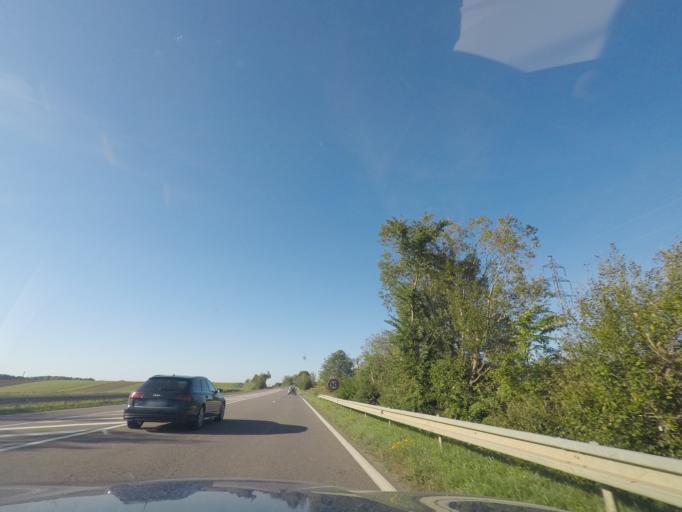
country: FR
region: Lorraine
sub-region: Departement de la Moselle
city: Hettange-Grande
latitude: 49.4404
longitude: 6.1689
